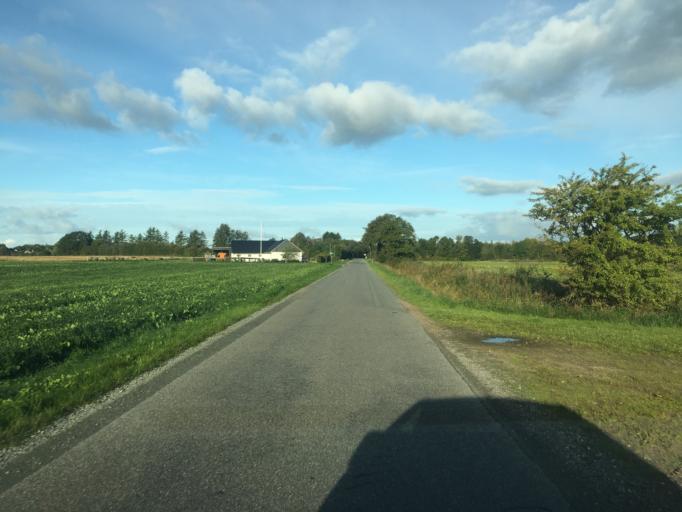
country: DK
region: South Denmark
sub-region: Tonder Kommune
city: Logumkloster
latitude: 55.0732
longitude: 8.9452
